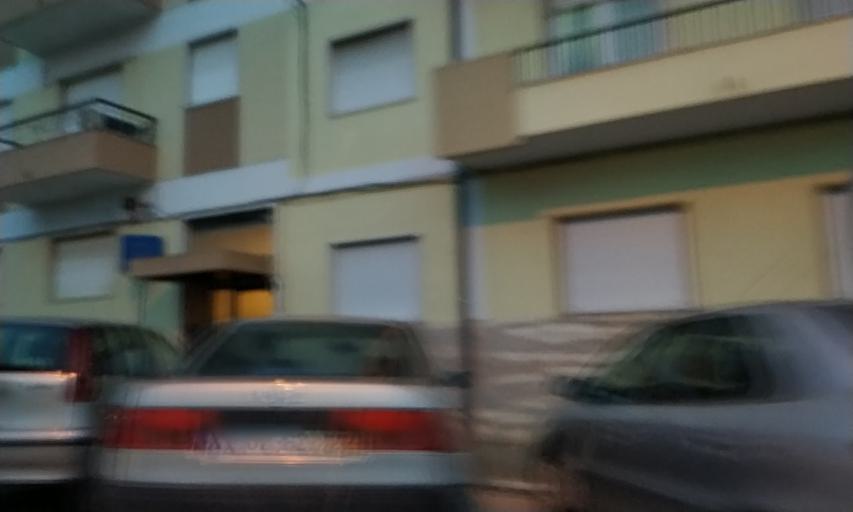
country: PT
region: Setubal
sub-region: Setubal
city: Setubal
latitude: 38.5288
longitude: -8.8791
